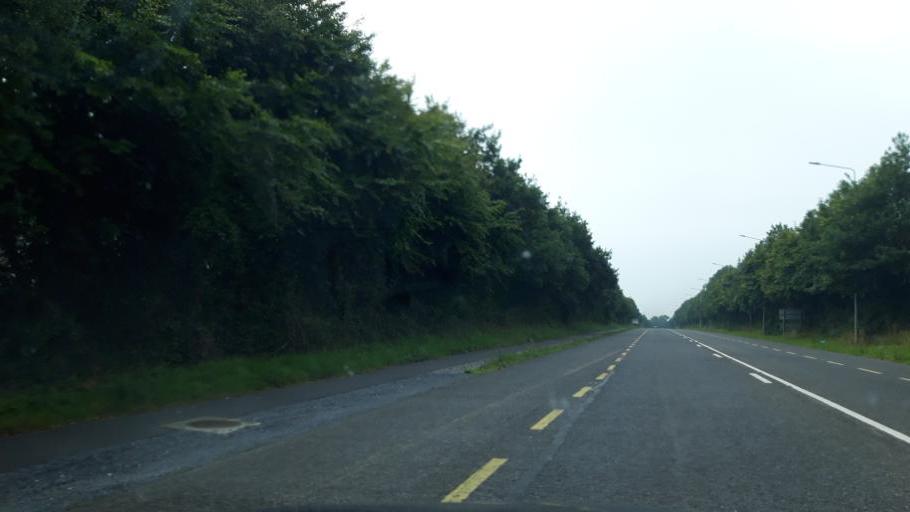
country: IE
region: Leinster
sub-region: Kilkenny
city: Callan
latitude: 52.5435
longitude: -7.3967
